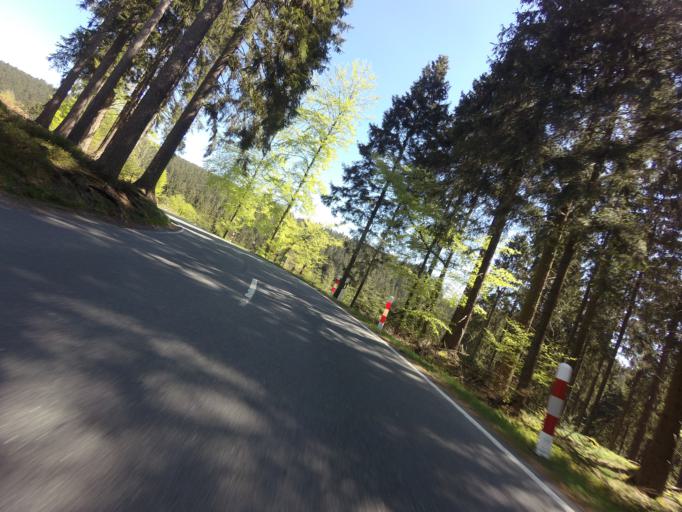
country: DE
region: North Rhine-Westphalia
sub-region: Regierungsbezirk Arnsberg
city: Erndtebruck
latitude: 51.0686
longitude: 8.2146
